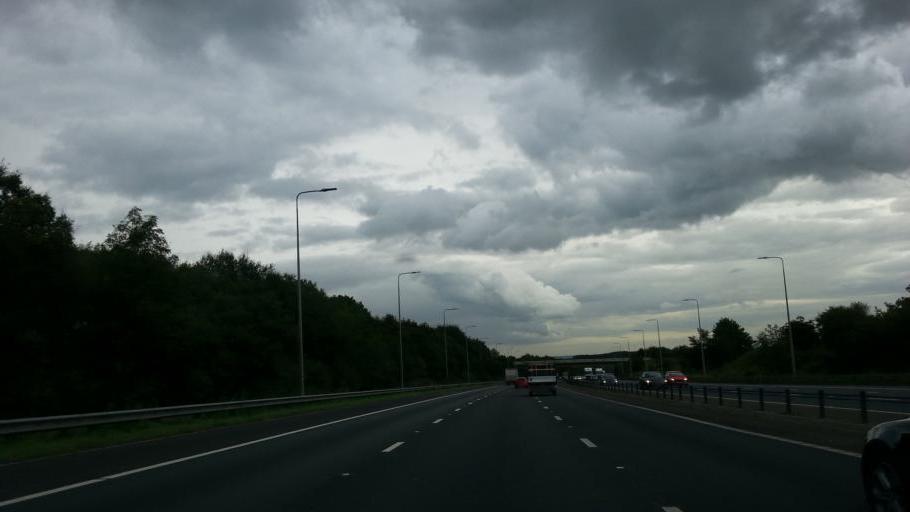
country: GB
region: England
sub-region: Kirklees
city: Linthwaite
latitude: 53.6497
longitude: -1.8860
